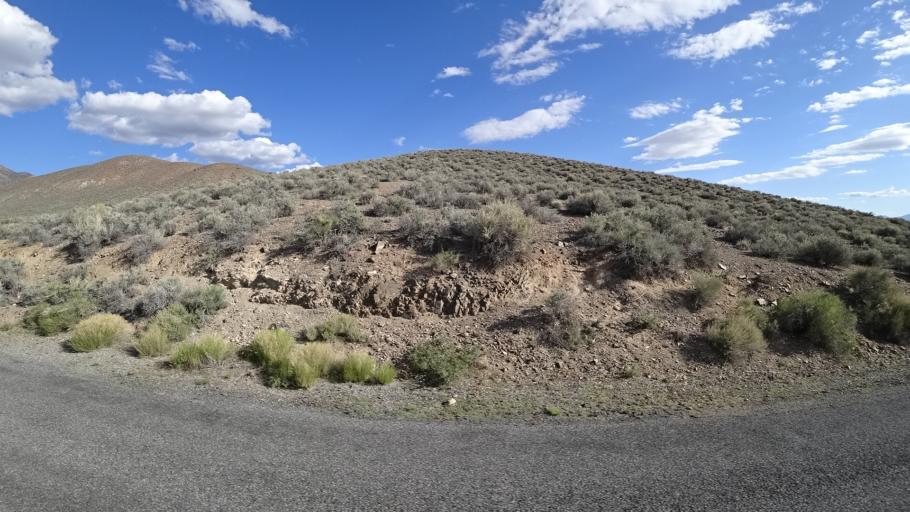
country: US
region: California
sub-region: San Bernardino County
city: Searles Valley
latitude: 36.3008
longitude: -117.1727
